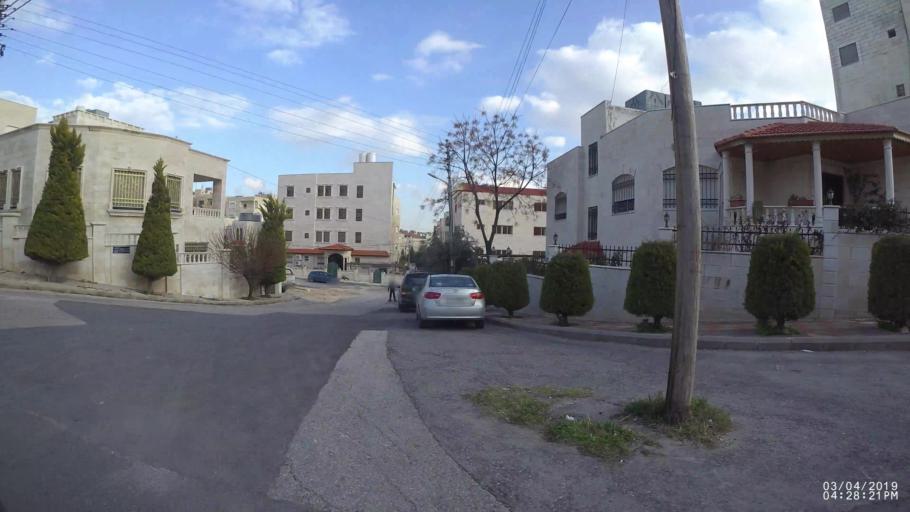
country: JO
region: Amman
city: Al Bunayyat ash Shamaliyah
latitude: 31.9141
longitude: 35.8885
